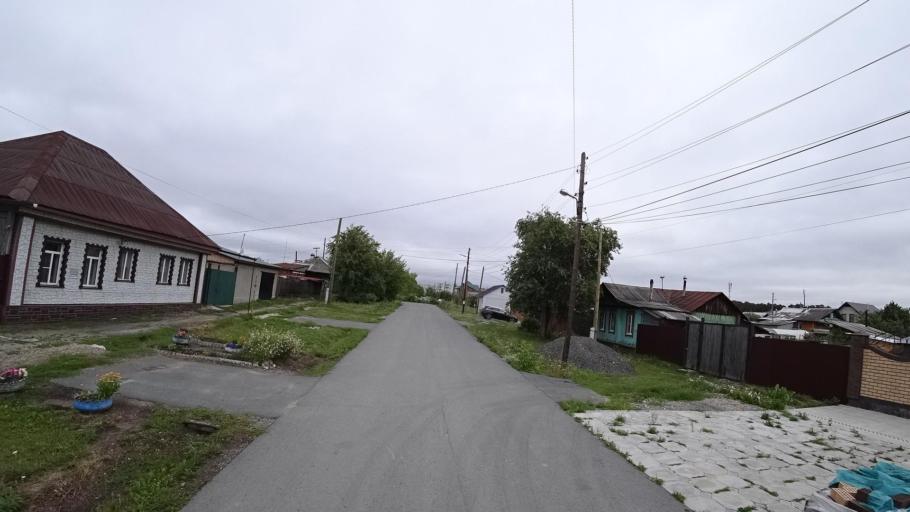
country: RU
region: Sverdlovsk
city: Kamyshlov
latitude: 56.8402
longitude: 62.7245
